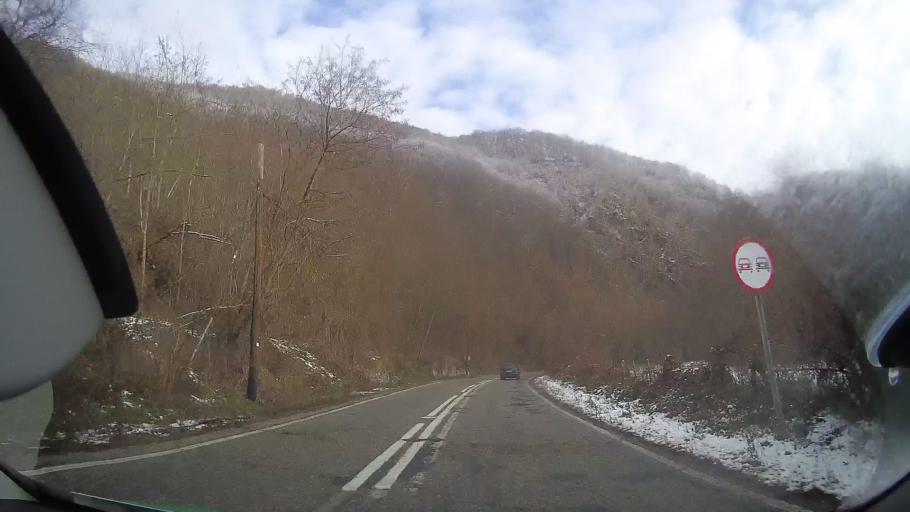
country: RO
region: Alba
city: Salciua de Sus
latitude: 46.4058
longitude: 23.3580
